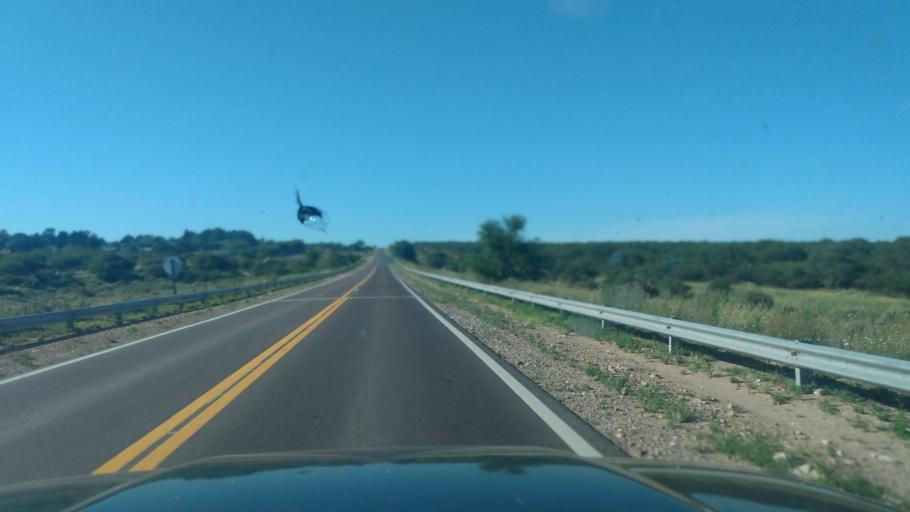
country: AR
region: La Pampa
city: Santa Rosa
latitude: -36.7198
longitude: -64.2830
